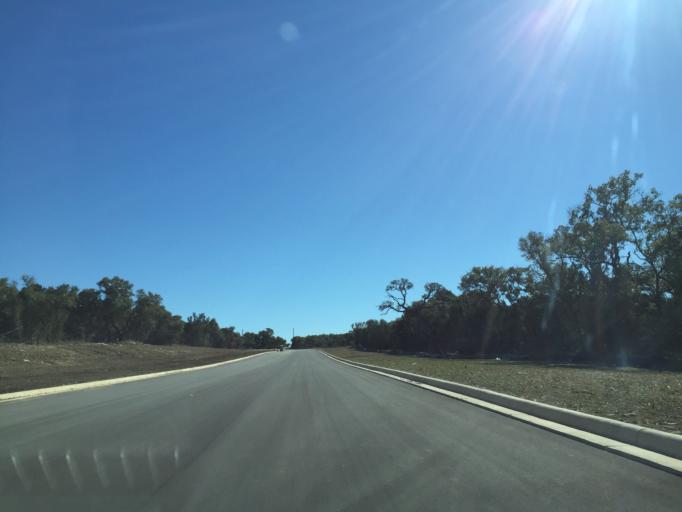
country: US
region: Texas
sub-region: Comal County
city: Bulverde
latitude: 29.7396
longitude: -98.4303
